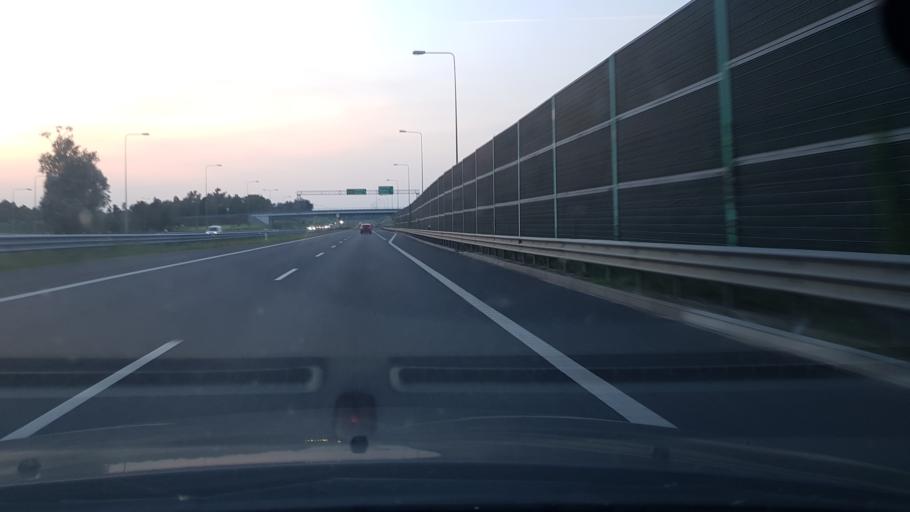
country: PL
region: Warmian-Masurian Voivodeship
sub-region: Powiat olsztynski
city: Olsztynek
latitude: 53.4976
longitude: 20.3144
